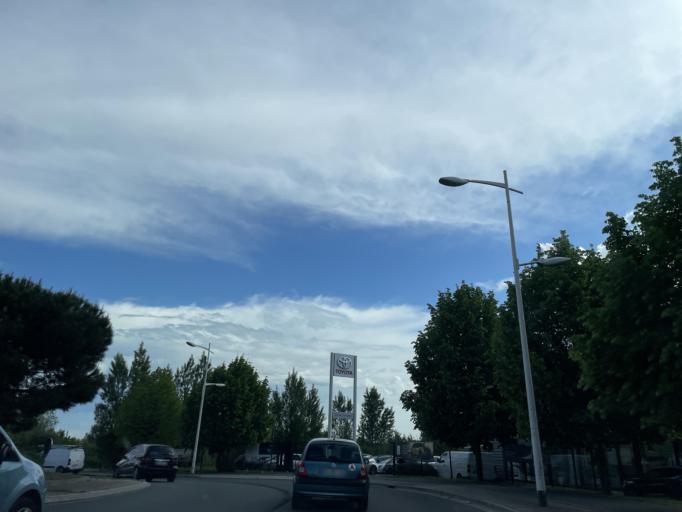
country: FR
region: Ile-de-France
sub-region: Departement du Val-d'Oise
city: Arnouville
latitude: 48.9722
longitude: 2.4193
